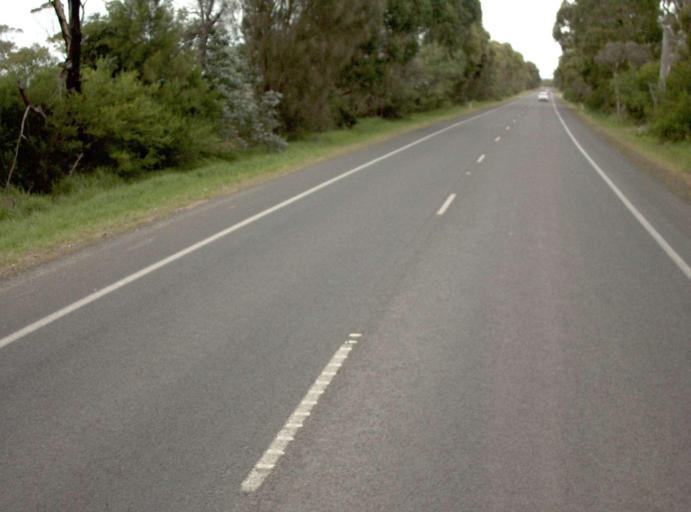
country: AU
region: Victoria
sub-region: Latrobe
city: Traralgon
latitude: -38.5471
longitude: 146.6959
